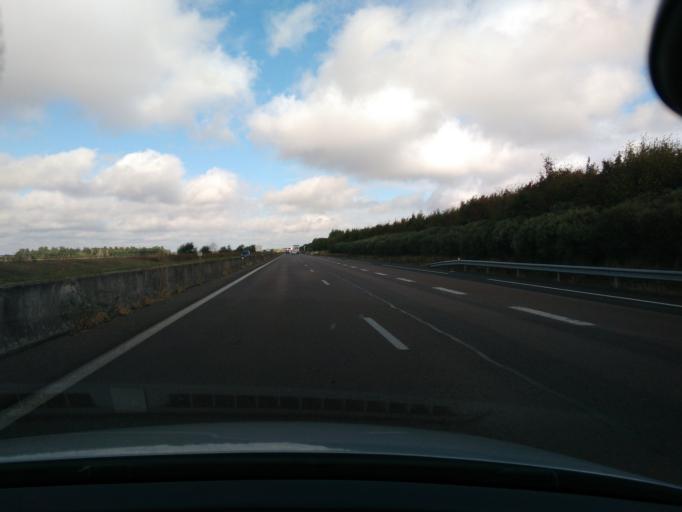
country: FR
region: Haute-Normandie
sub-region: Departement de l'Eure
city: Damville
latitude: 48.8718
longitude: 1.1760
